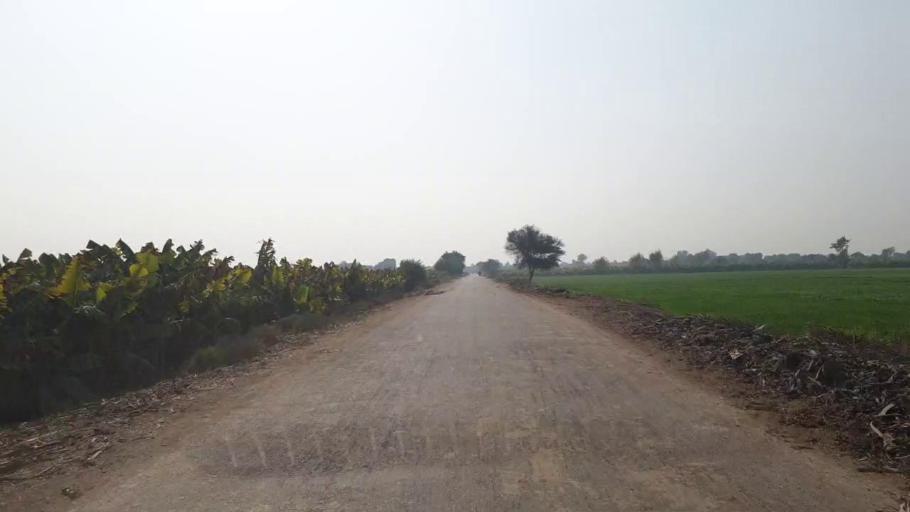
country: PK
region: Sindh
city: Hala
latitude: 25.8683
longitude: 68.4303
